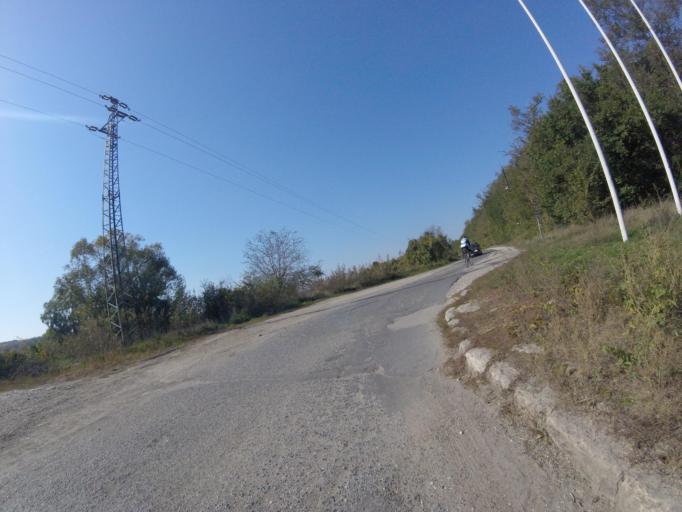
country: HU
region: Fejer
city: Etyek
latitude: 47.4883
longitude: 18.7652
